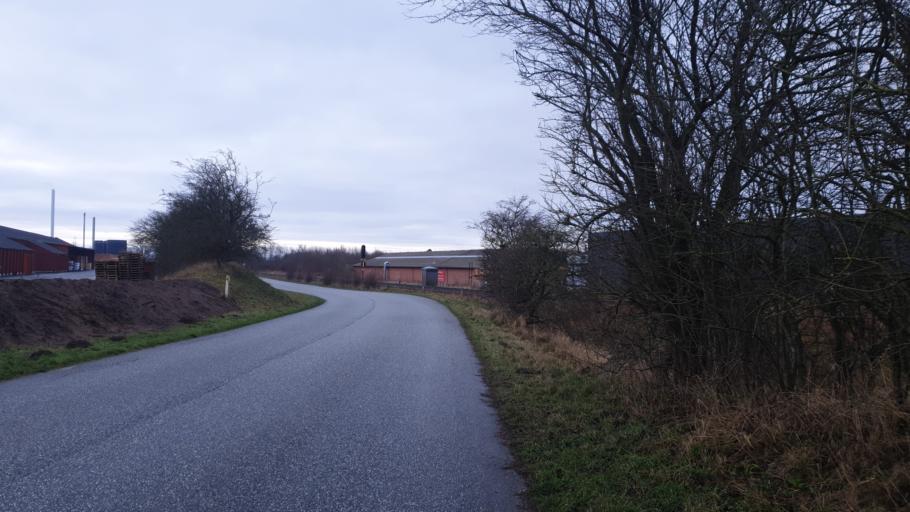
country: DK
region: Central Jutland
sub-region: Hedensted Kommune
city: Hedensted
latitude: 55.7784
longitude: 9.6999
